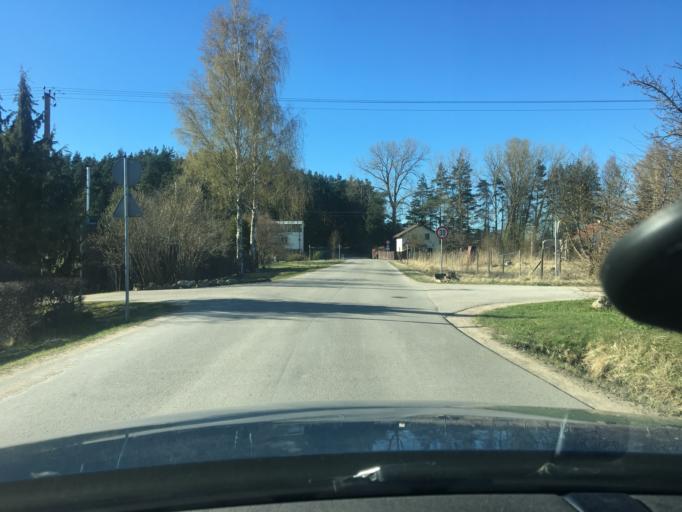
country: LV
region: Kekava
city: Kekava
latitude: 56.8543
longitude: 24.2565
